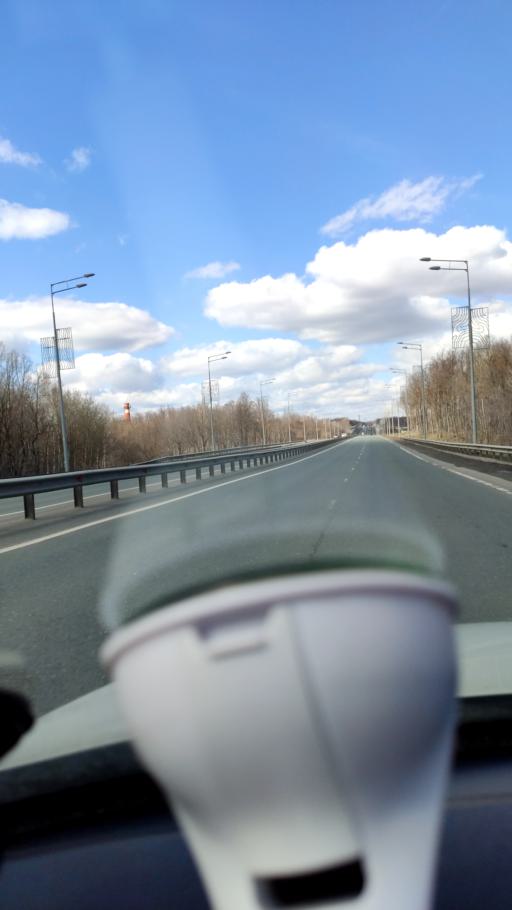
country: RU
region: Samara
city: Novosemeykino
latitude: 53.3331
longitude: 50.2314
